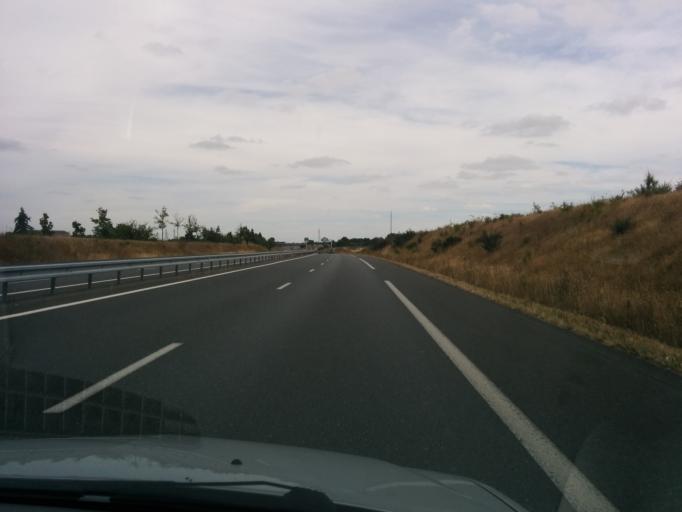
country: FR
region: Poitou-Charentes
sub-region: Departement des Deux-Sevres
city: Saint-Pierre-des-Echaubrognes
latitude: 46.9318
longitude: -0.7366
